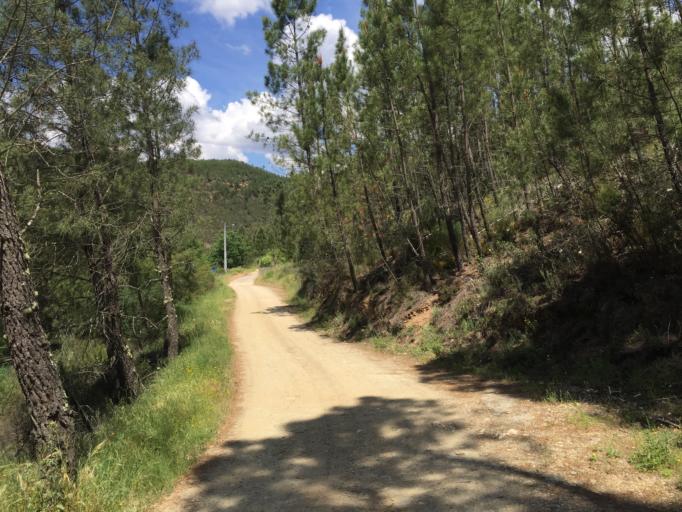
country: PT
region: Coimbra
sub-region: Pampilhosa da Serra
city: Pampilhosa da Serra
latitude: 40.0794
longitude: -7.7892
